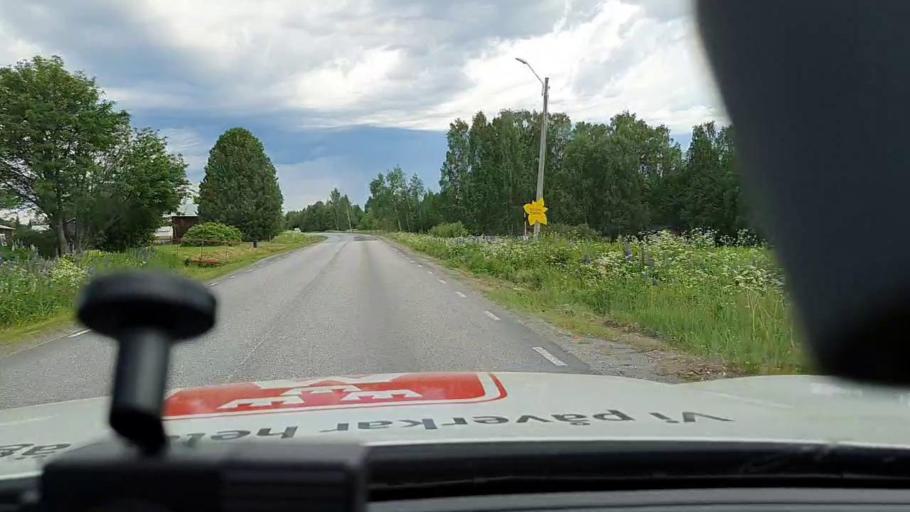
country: SE
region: Norrbotten
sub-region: Bodens Kommun
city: Saevast
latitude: 65.7666
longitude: 21.6907
